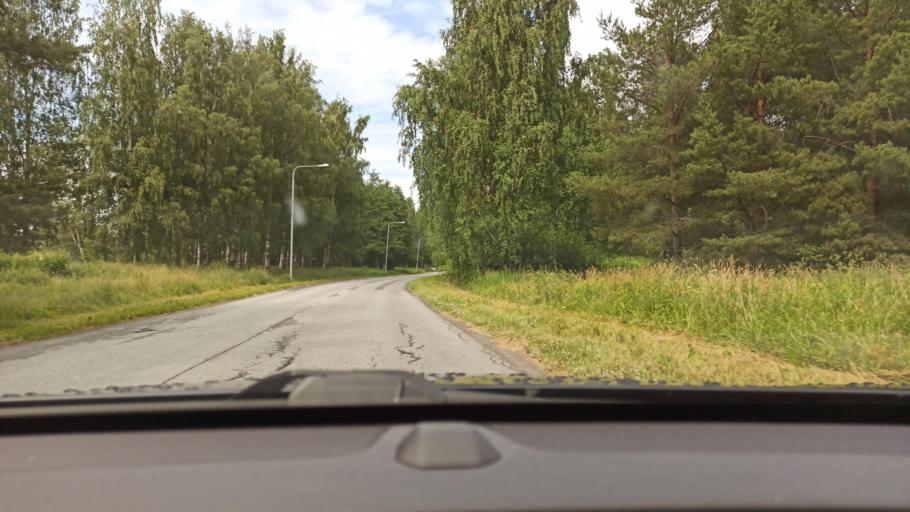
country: FI
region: Satakunta
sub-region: Pori
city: Pori
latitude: 61.5078
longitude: 21.7757
